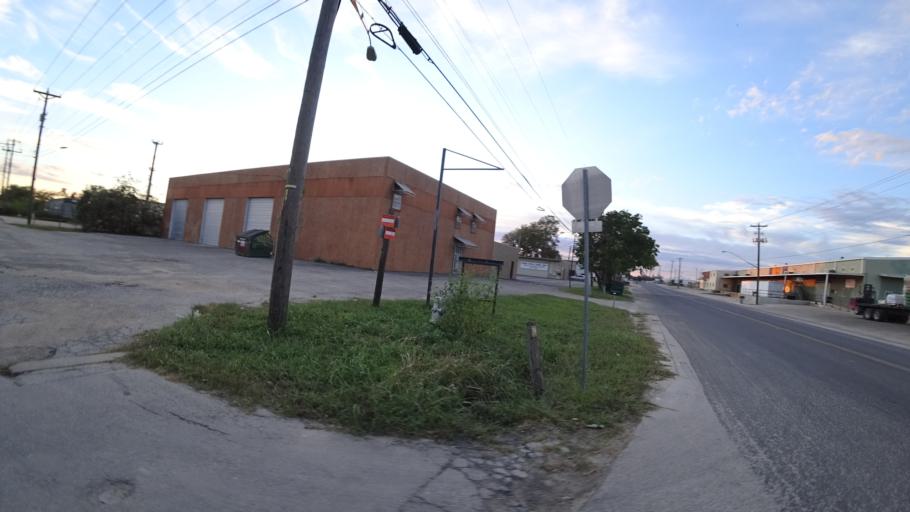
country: US
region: Texas
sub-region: Travis County
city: Austin
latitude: 30.2168
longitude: -97.7582
